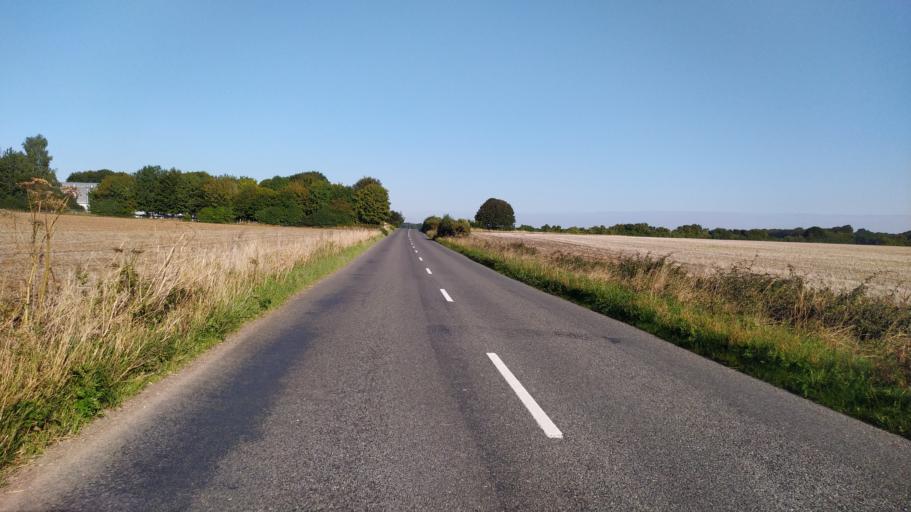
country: GB
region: England
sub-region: Hampshire
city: Abbotts Ann
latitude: 51.1449
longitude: -1.5364
